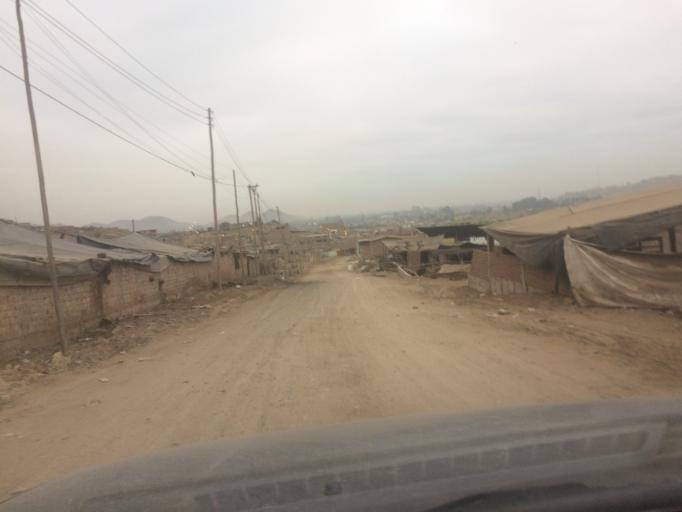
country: PE
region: Lima
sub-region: Lima
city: Cieneguilla
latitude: -12.2240
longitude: -76.8947
